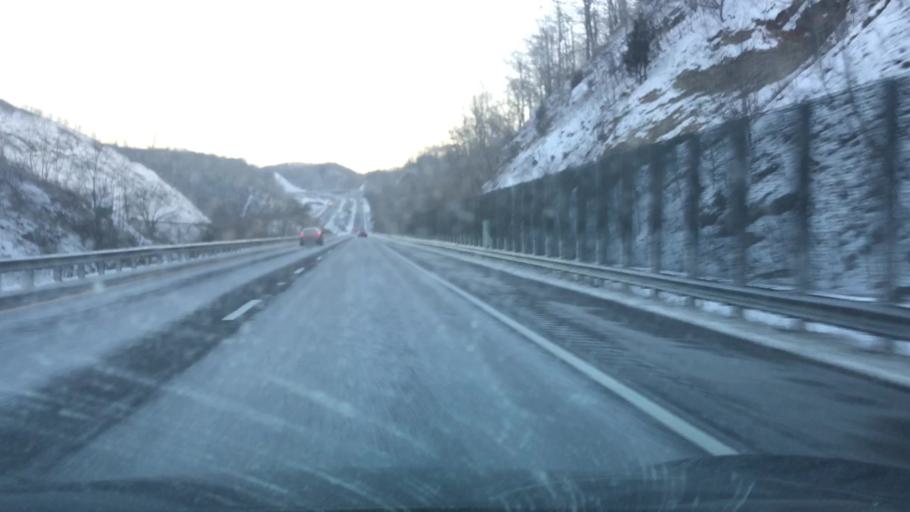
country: US
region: Virginia
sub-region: Montgomery County
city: Shawsville
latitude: 37.1870
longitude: -80.2819
